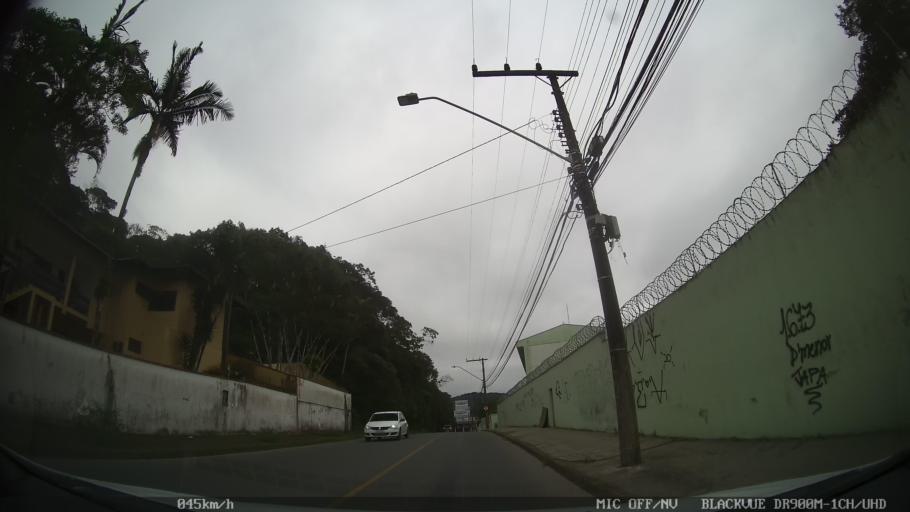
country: BR
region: Santa Catarina
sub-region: Joinville
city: Joinville
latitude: -26.2638
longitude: -48.8530
